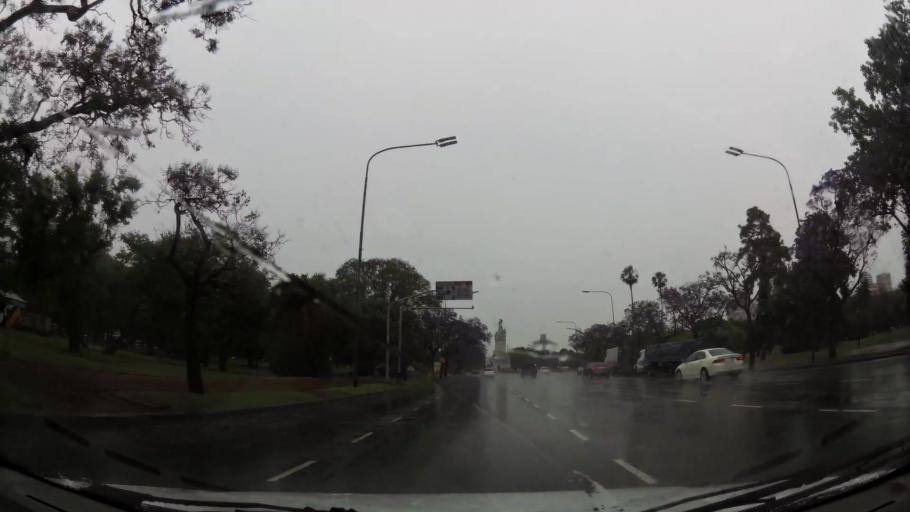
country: AR
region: Buenos Aires F.D.
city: Retiro
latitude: -34.5737
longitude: -58.4137
